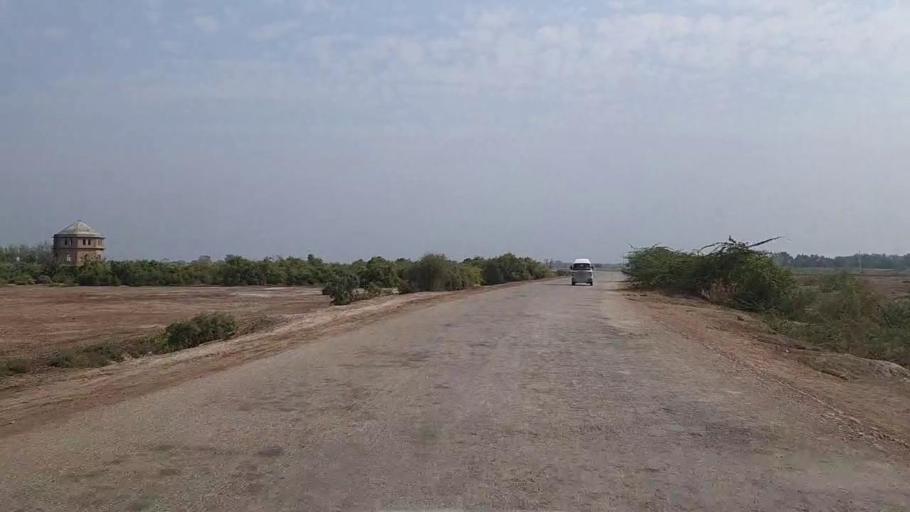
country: PK
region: Sindh
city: Mirwah Gorchani
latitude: 25.4150
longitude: 69.0338
